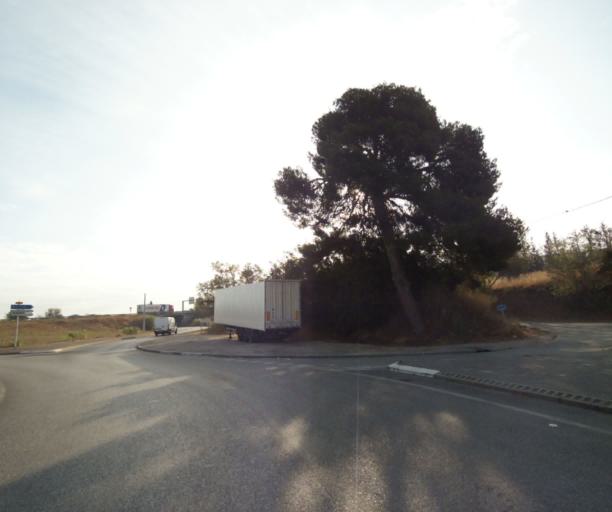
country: FR
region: Provence-Alpes-Cote d'Azur
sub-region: Departement des Bouches-du-Rhone
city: Les Pennes-Mirabeau
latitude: 43.4158
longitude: 5.2748
